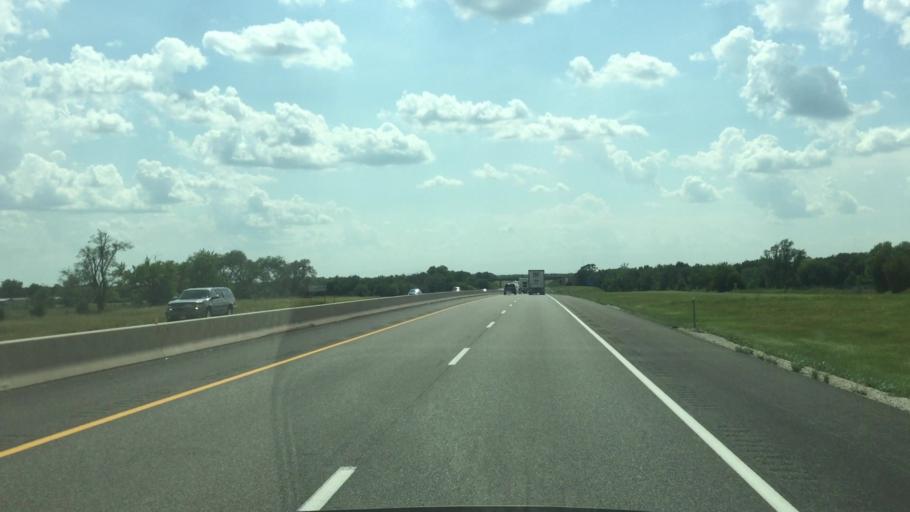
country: US
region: Kansas
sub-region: Butler County
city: Towanda
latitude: 37.7416
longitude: -97.0576
